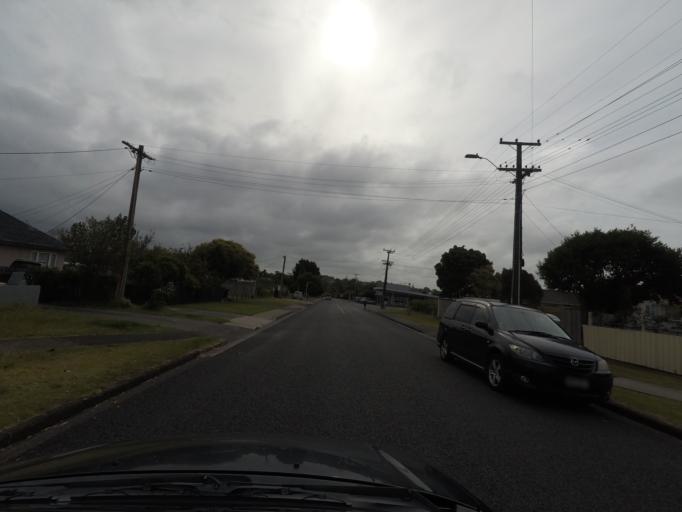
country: NZ
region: Auckland
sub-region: Auckland
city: Rosebank
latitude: -36.8948
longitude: 174.6670
